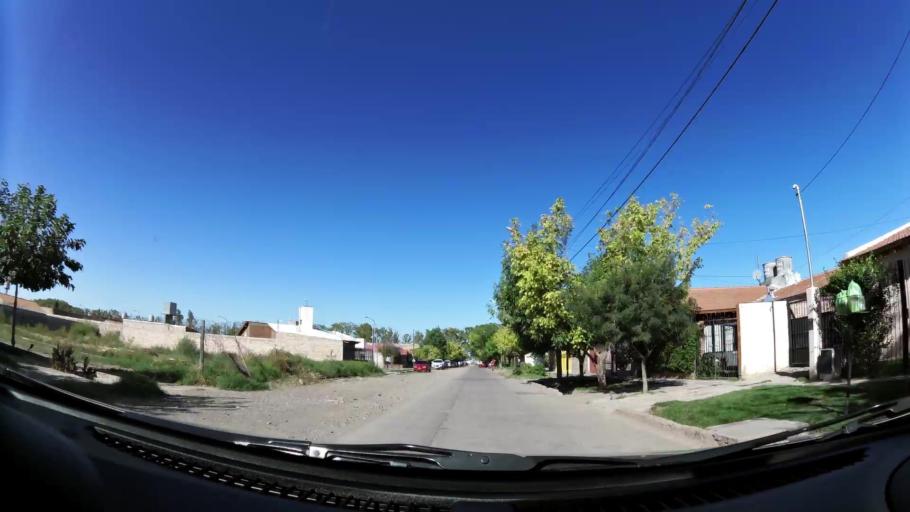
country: AR
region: Mendoza
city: Las Heras
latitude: -32.8476
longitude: -68.8304
